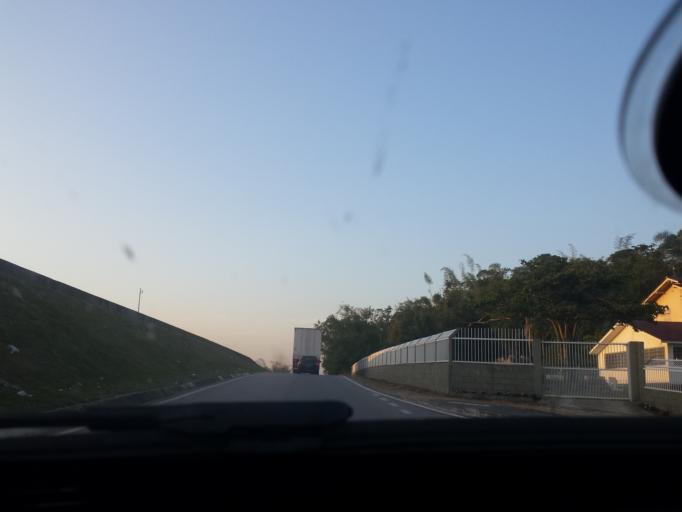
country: BR
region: Santa Catarina
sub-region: Florianopolis
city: Pantano do Sul
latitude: -27.8468
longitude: -48.6371
